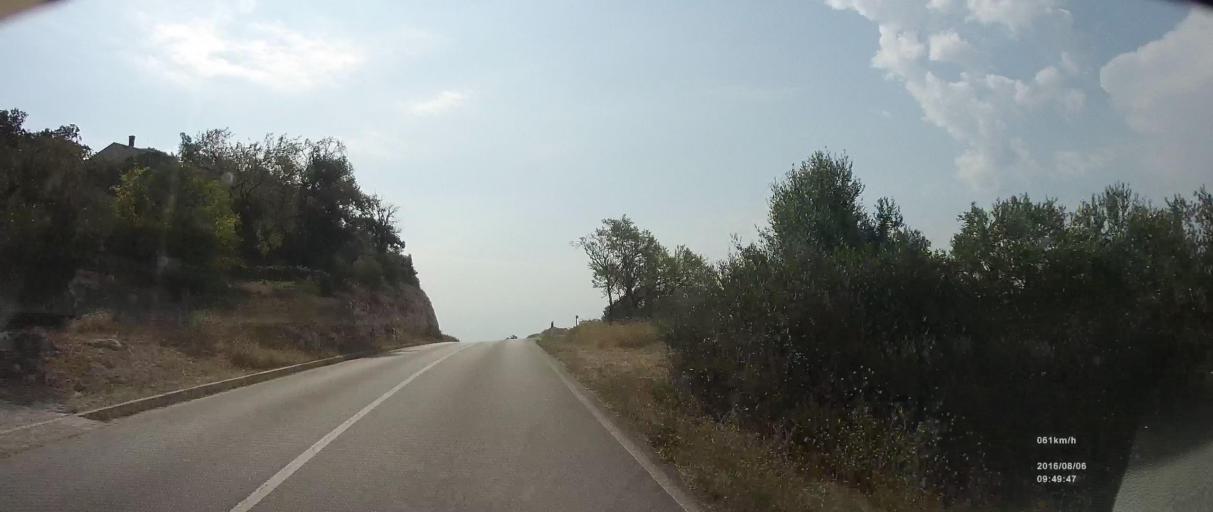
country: HR
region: Dubrovacko-Neretvanska
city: Blato
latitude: 42.7360
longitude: 17.5453
